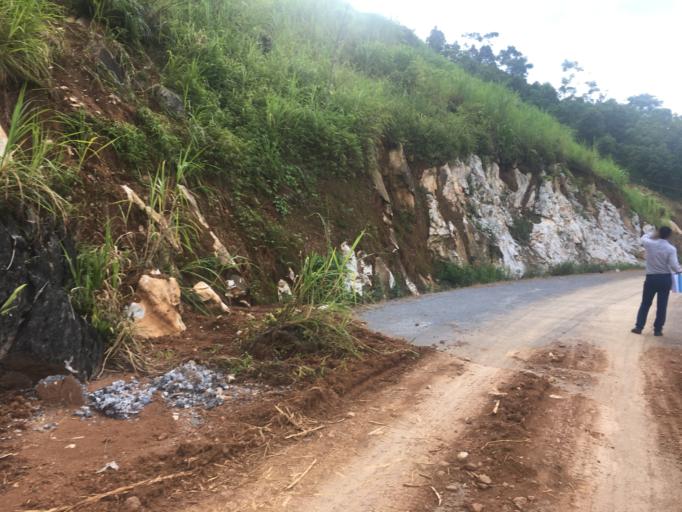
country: VN
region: Ha Giang
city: Thanh Pho Ha Giang
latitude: 22.9005
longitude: 105.0226
